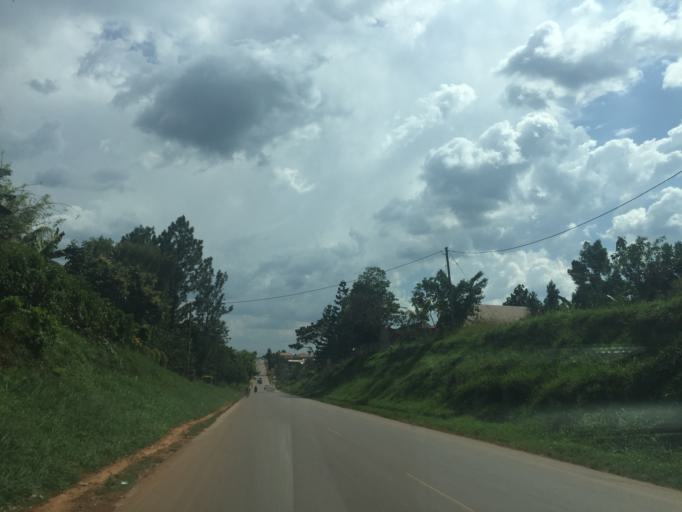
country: UG
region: Central Region
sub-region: Luwero District
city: Wobulenzi
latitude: 0.7268
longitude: 32.5281
